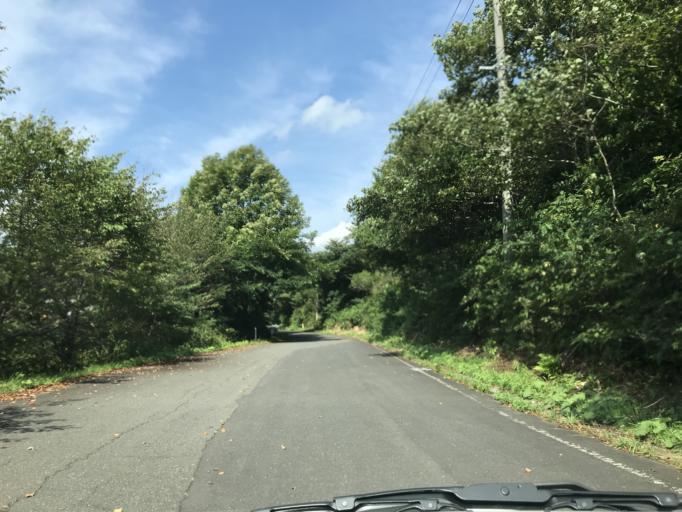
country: JP
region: Iwate
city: Ofunato
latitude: 38.9863
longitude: 141.4563
